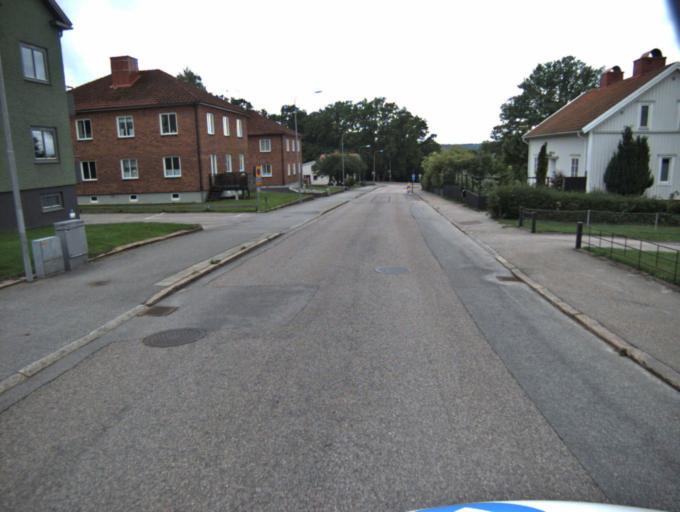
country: SE
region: Vaestra Goetaland
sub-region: Ulricehamns Kommun
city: Ulricehamn
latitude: 57.7863
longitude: 13.4157
